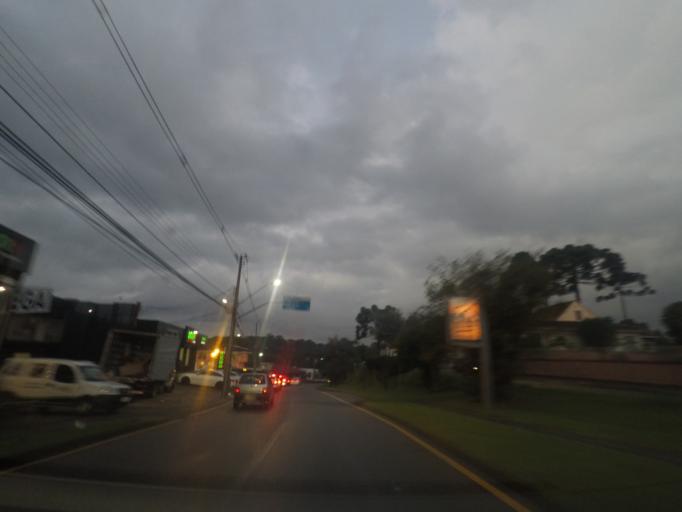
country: BR
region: Parana
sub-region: Curitiba
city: Curitiba
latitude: -25.4093
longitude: -49.3232
